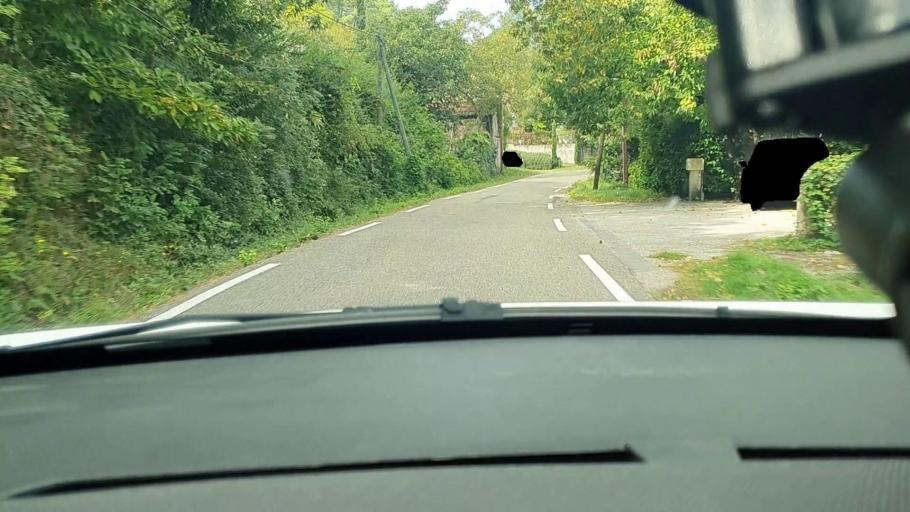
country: FR
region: Languedoc-Roussillon
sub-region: Departement du Gard
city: Besseges
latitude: 44.3025
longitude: 4.0148
